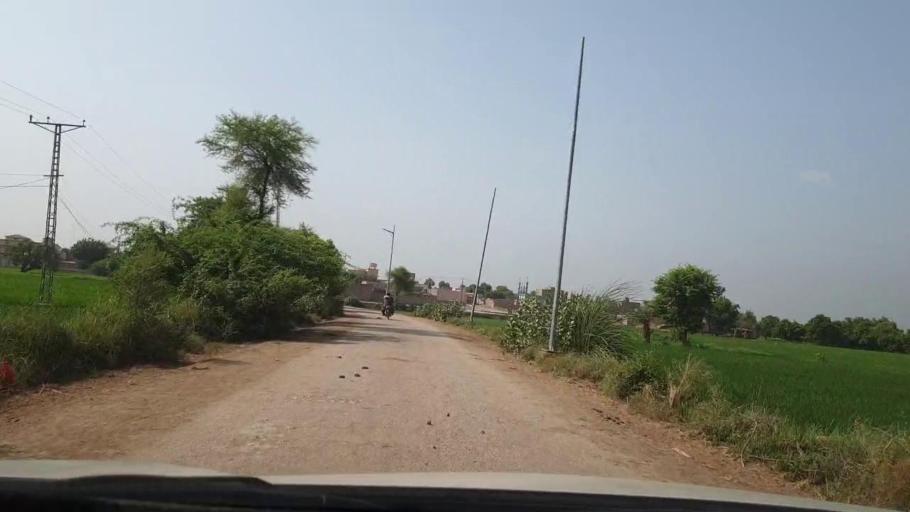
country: PK
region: Sindh
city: Larkana
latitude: 27.4619
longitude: 68.2296
